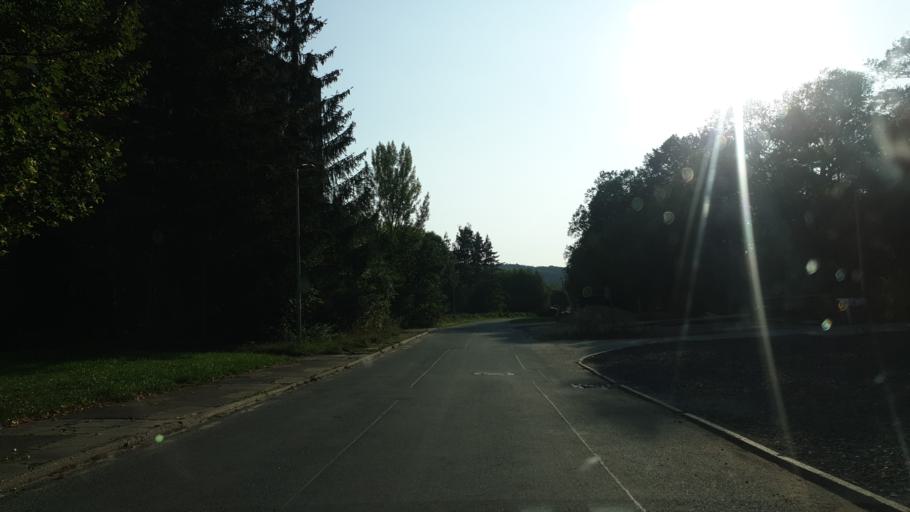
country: DE
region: Thuringia
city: Hartmannsdorf
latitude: 50.9616
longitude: 11.9796
